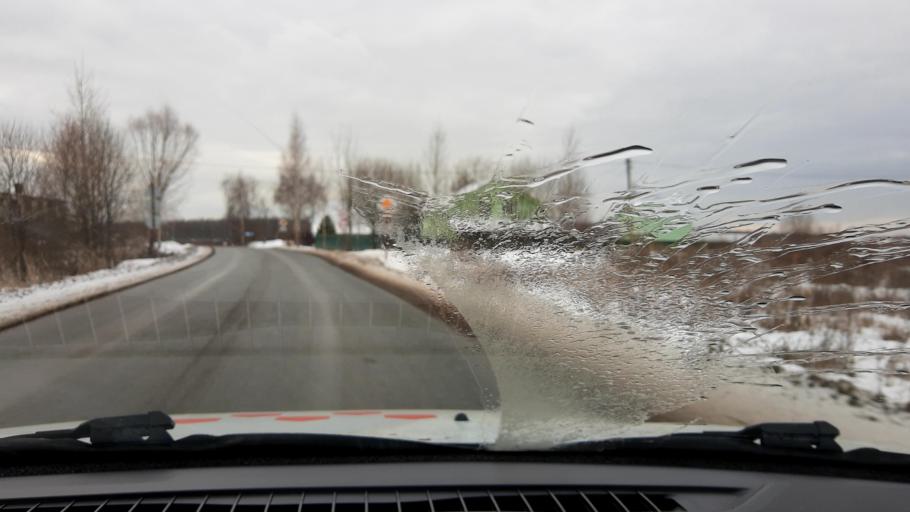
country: RU
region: Nizjnij Novgorod
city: Neklyudovo
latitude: 56.4227
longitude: 43.9565
